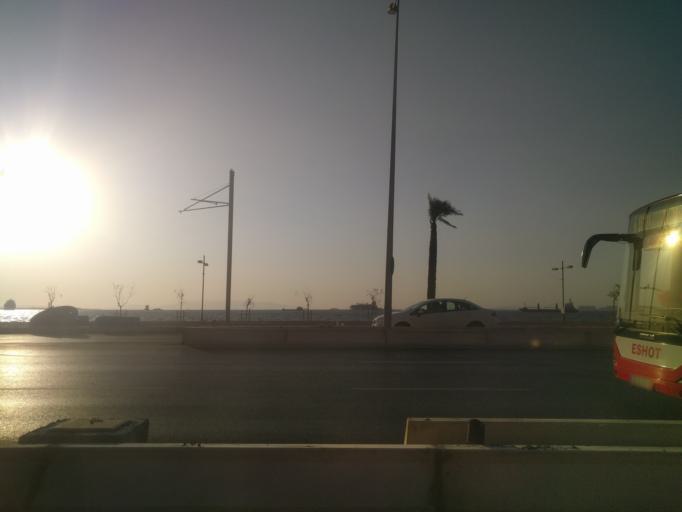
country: TR
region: Izmir
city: Izmir
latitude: 38.4135
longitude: 27.1215
